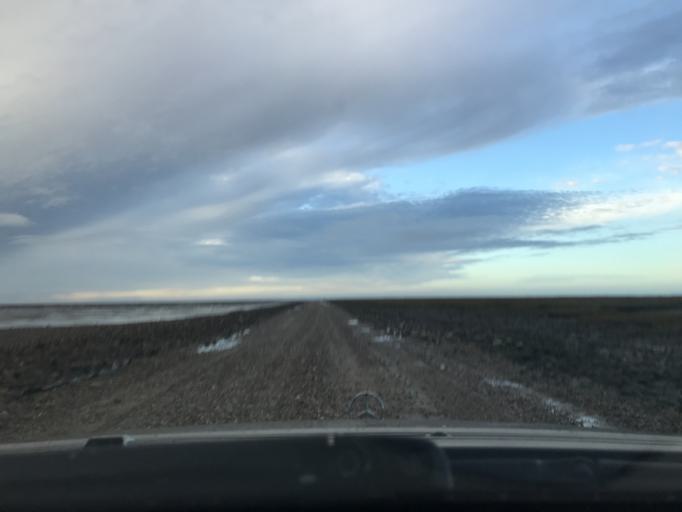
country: DK
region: South Denmark
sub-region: Esbjerg Kommune
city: Ribe
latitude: 55.3087
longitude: 8.6488
